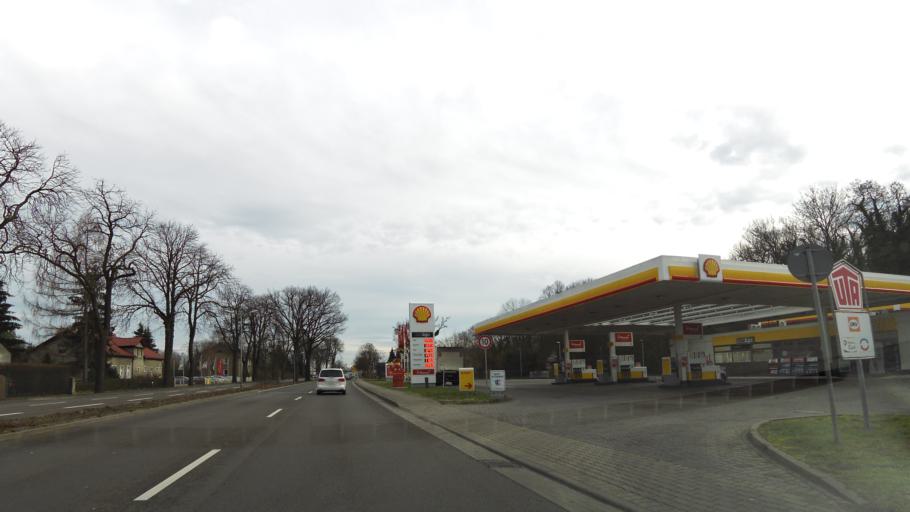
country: DE
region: Brandenburg
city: Schoneiche
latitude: 52.5004
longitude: 13.7354
